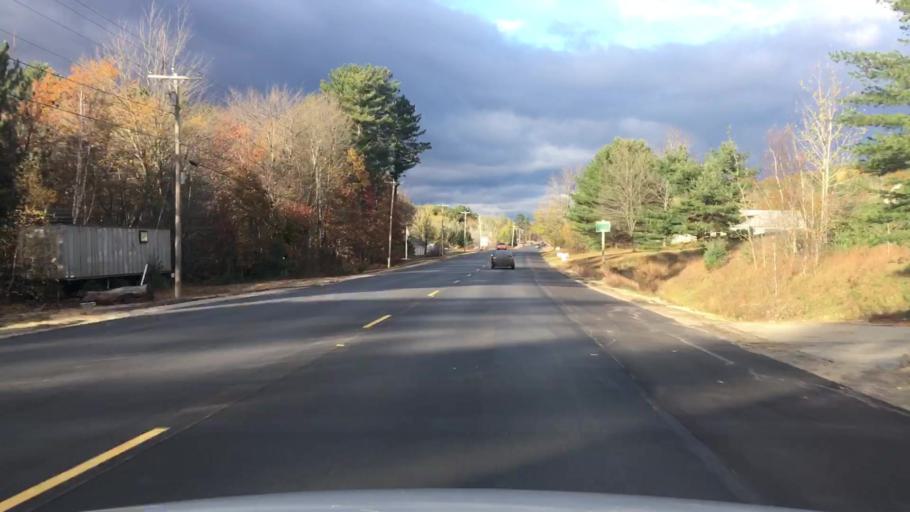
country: US
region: Maine
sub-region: Androscoggin County
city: Livermore
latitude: 44.3602
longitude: -70.2548
